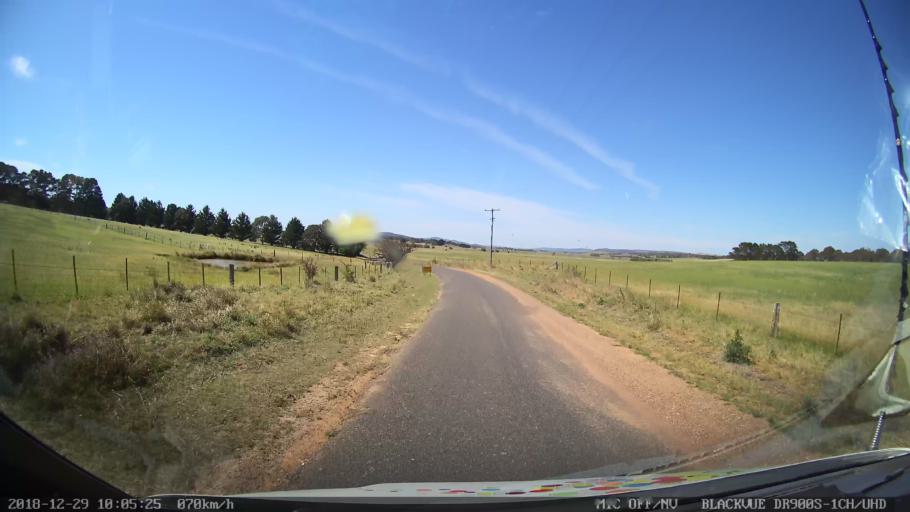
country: AU
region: New South Wales
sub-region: Goulburn Mulwaree
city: Goulburn
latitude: -34.8329
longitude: 149.4532
